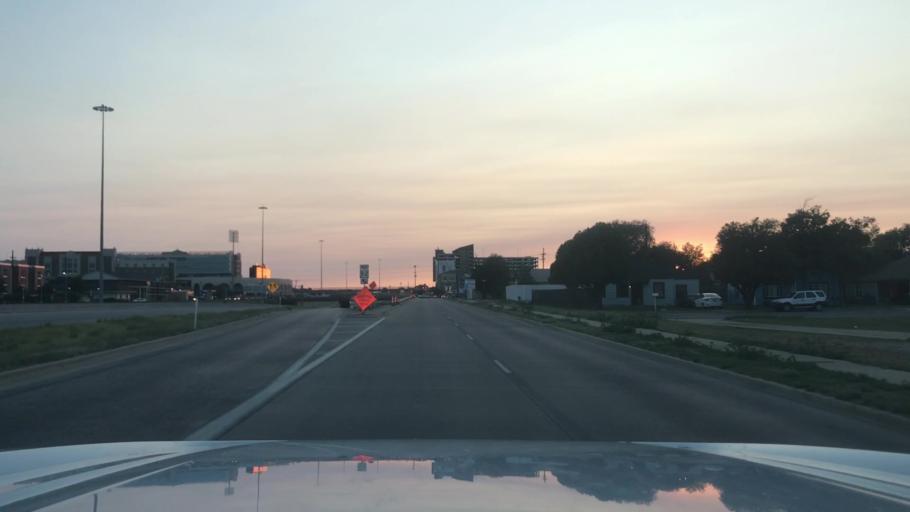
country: US
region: Texas
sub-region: Lubbock County
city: Lubbock
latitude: 33.5931
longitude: -101.8656
